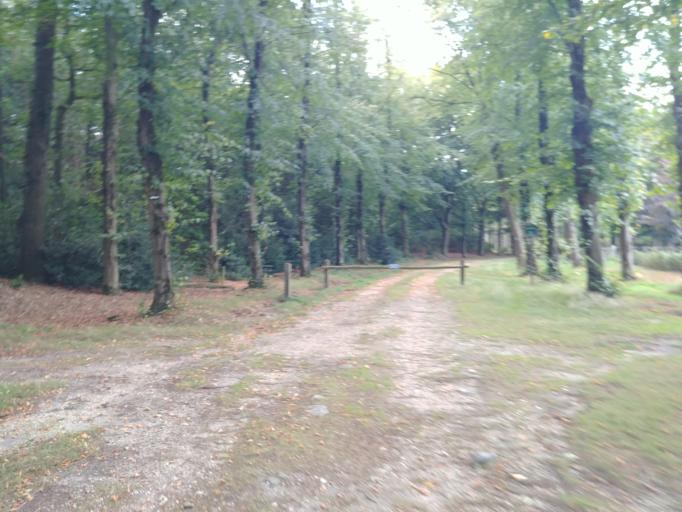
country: NL
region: Utrecht
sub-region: Gemeente Utrechtse Heuvelrug
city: Maarn
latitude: 52.0496
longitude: 5.3658
